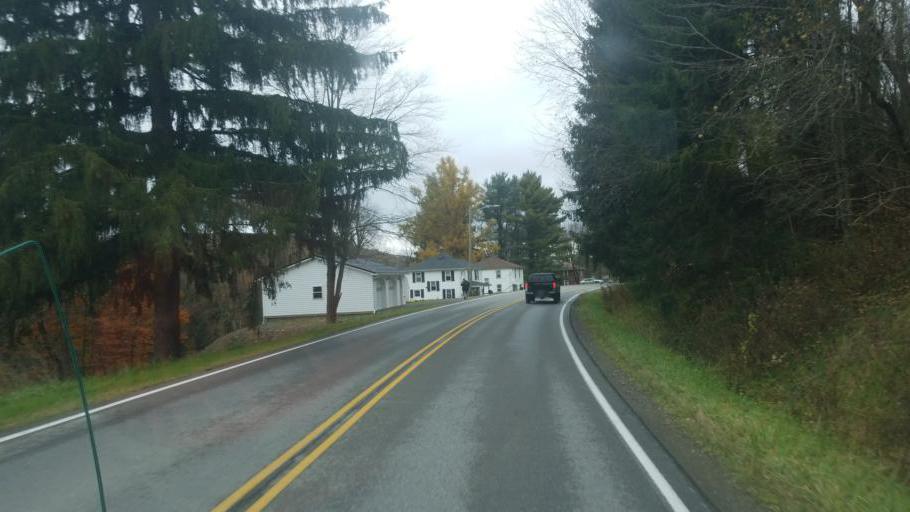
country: US
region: Pennsylvania
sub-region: Elk County
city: Saint Marys
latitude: 41.3227
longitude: -78.6357
